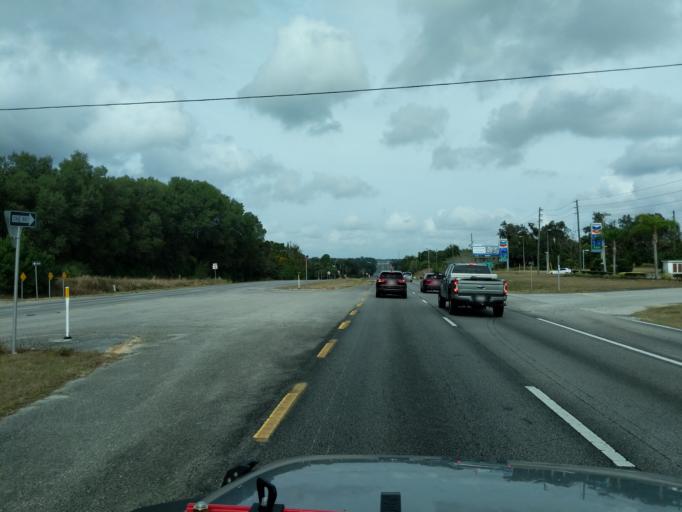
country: US
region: Florida
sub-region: Orange County
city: Tangerine
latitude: 28.7741
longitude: -81.6242
